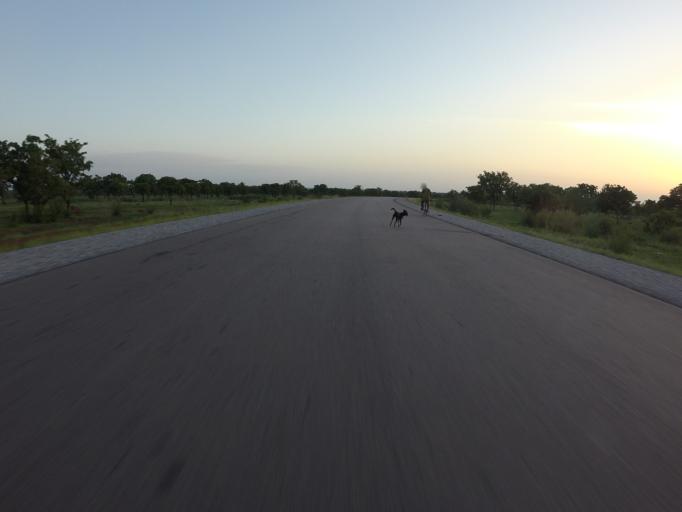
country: GH
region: Northern
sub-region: Yendi
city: Yendi
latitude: 9.9398
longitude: -0.1692
